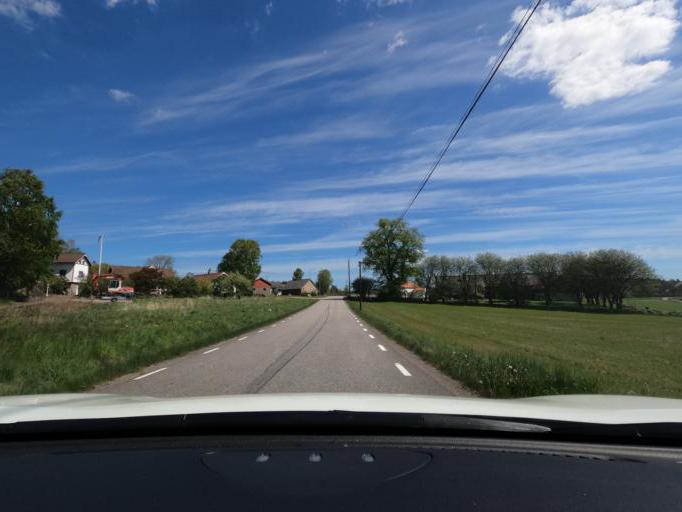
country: SE
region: Halland
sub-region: Kungsbacka Kommun
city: Fjaeras kyrkby
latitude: 57.3943
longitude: 12.2616
